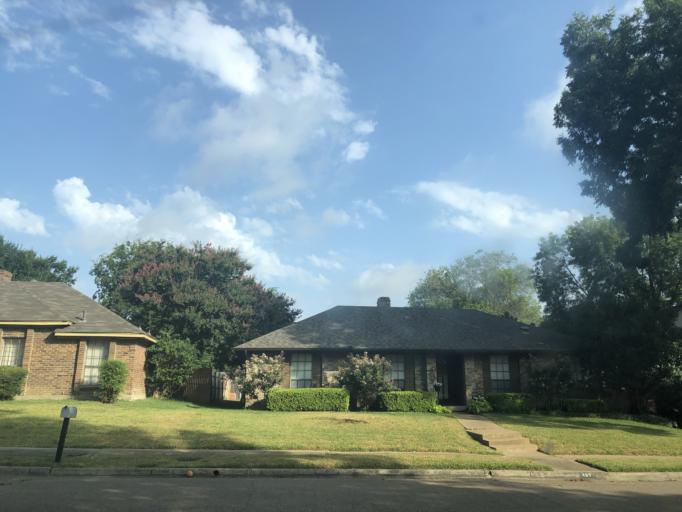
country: US
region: Texas
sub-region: Dallas County
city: Garland
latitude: 32.8595
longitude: -96.6280
